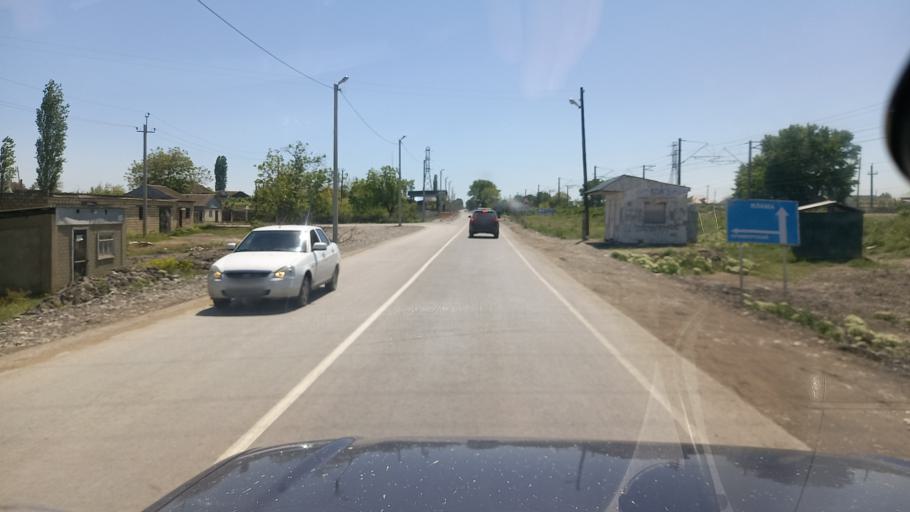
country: RU
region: Dagestan
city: Samur
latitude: 41.8089
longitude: 48.5152
